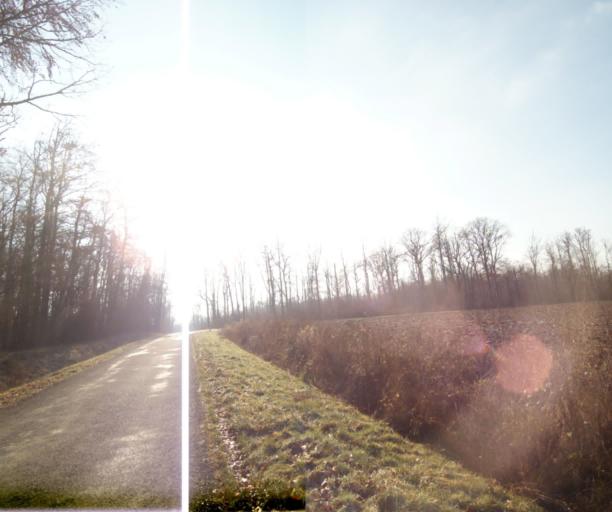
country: FR
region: Champagne-Ardenne
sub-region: Departement de la Haute-Marne
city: Wassy
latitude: 48.4598
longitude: 4.9384
